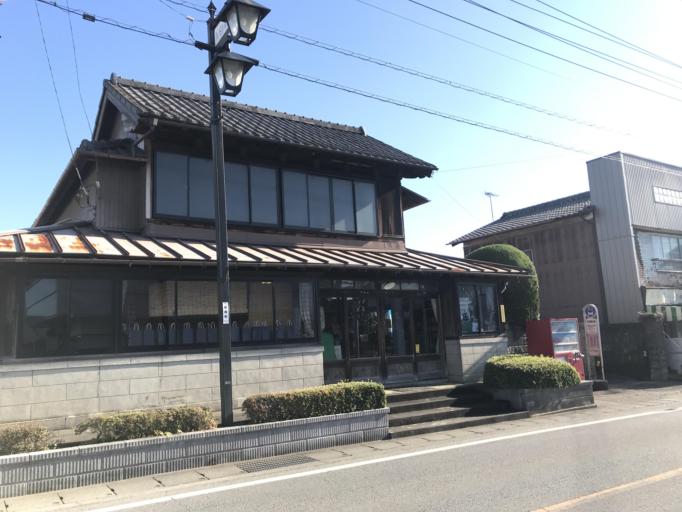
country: JP
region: Ibaraki
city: Sakai
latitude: 36.1145
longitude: 139.7968
